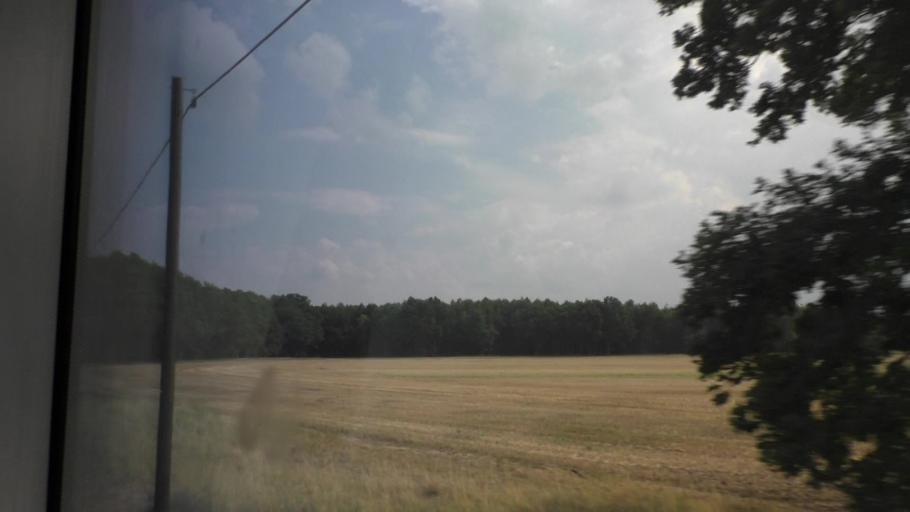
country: DE
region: Brandenburg
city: Storkow
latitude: 52.2799
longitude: 13.8570
